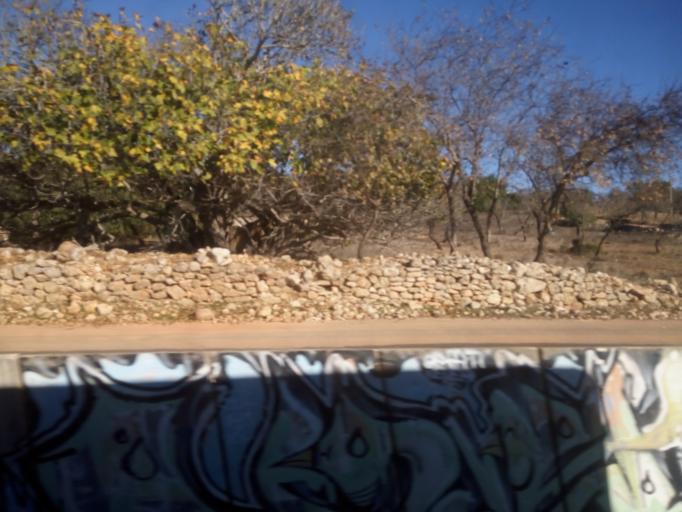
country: PT
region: Faro
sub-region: Albufeira
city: Ferreiras
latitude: 37.1564
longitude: -8.2492
